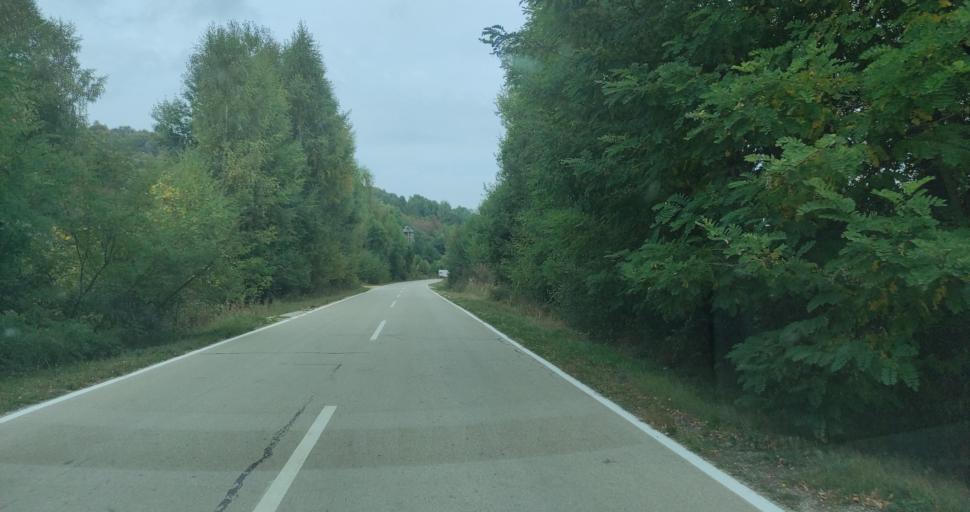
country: RS
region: Central Serbia
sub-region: Jablanicki Okrug
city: Crna Trava
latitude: 42.7094
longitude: 22.3280
